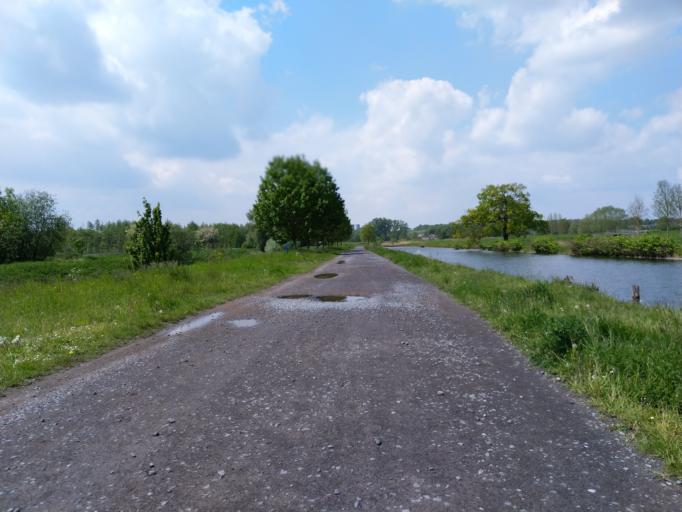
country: BE
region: Wallonia
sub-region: Province du Hainaut
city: Roeulx
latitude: 50.4730
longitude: 4.0633
